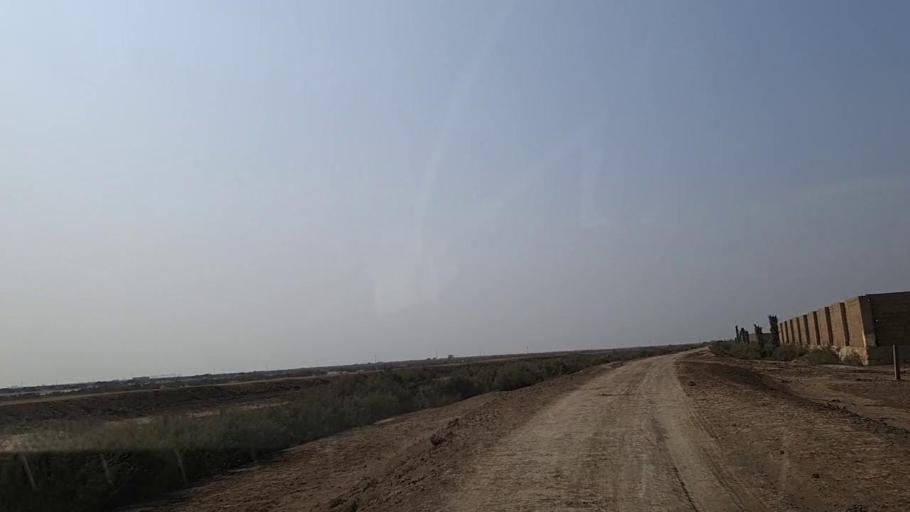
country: PK
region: Sindh
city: Gharo
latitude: 24.6735
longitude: 67.7114
